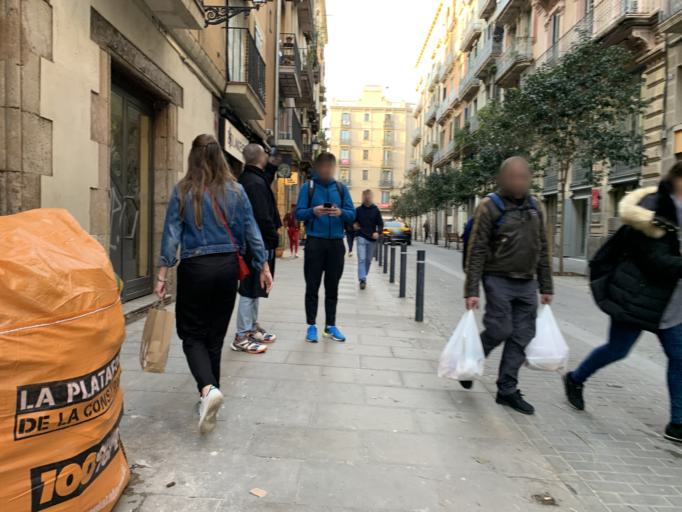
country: ES
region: Catalonia
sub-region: Provincia de Barcelona
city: Ciutat Vella
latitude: 41.3859
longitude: 2.1824
